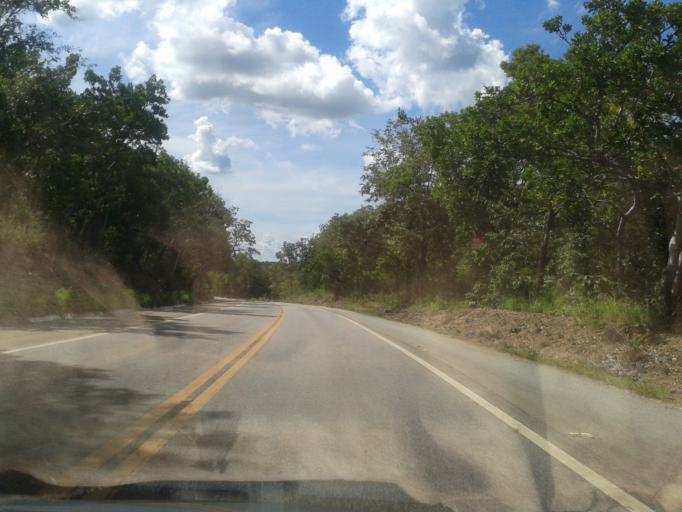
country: BR
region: Goias
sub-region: Itapuranga
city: Itapuranga
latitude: -15.4954
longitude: -50.3104
